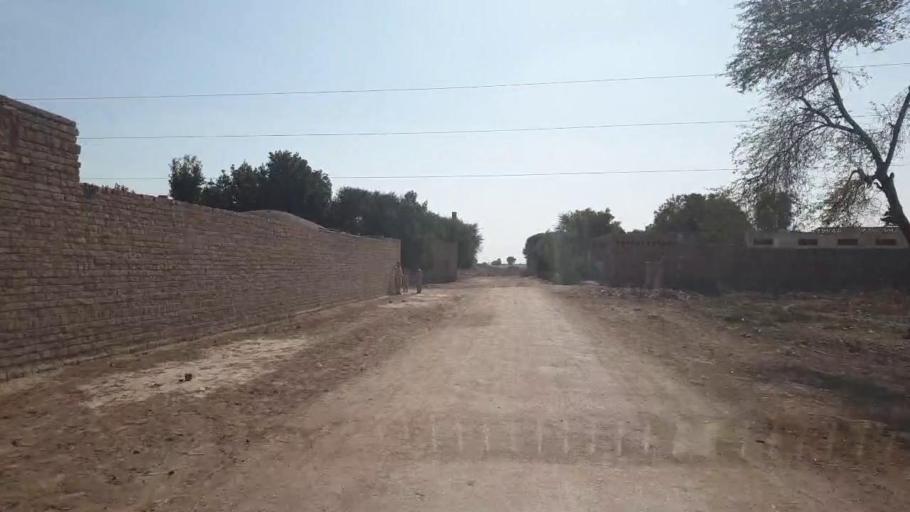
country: PK
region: Sindh
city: Tando Allahyar
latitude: 25.4281
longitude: 68.6941
